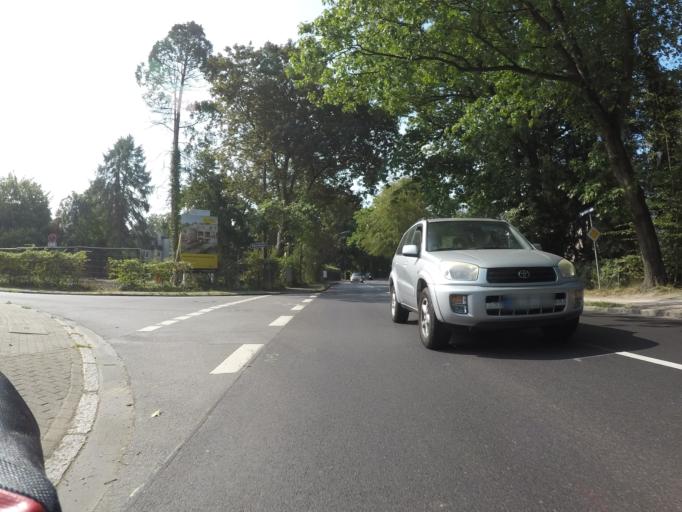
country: DE
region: Hamburg
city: Wellingsbuettel
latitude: 53.6453
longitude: 10.0862
